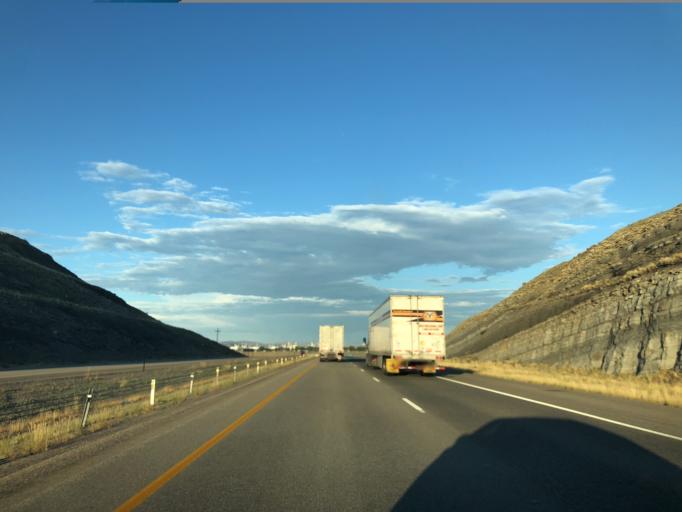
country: US
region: Wyoming
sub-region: Carbon County
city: Rawlins
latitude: 41.7825
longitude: -107.1455
